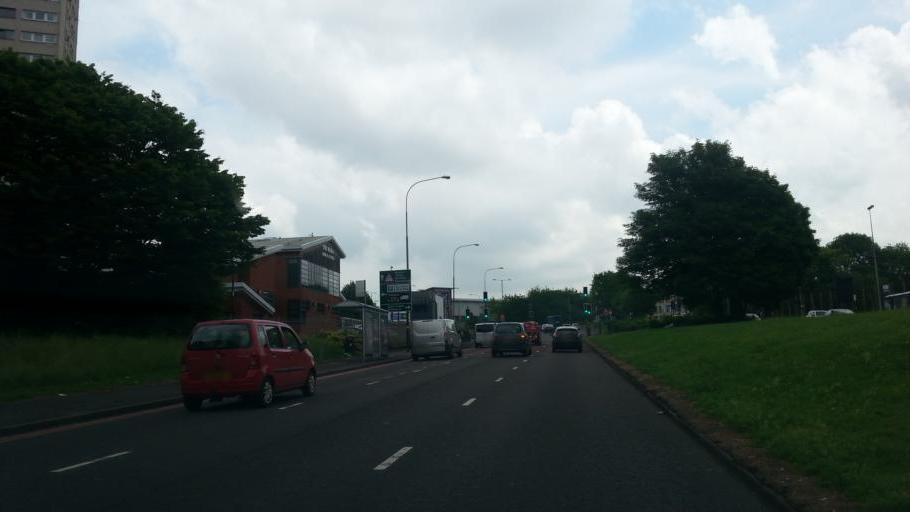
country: GB
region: England
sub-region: City and Borough of Birmingham
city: Birmingham
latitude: 52.4642
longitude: -1.8900
